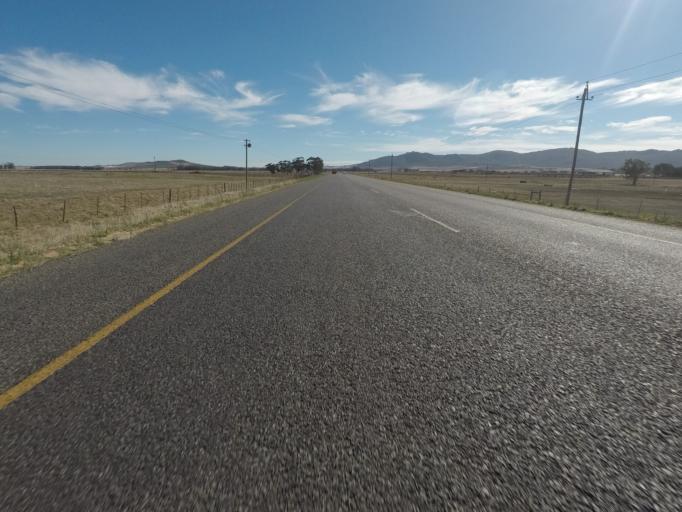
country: ZA
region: Western Cape
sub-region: West Coast District Municipality
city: Malmesbury
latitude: -33.6350
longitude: 18.7198
